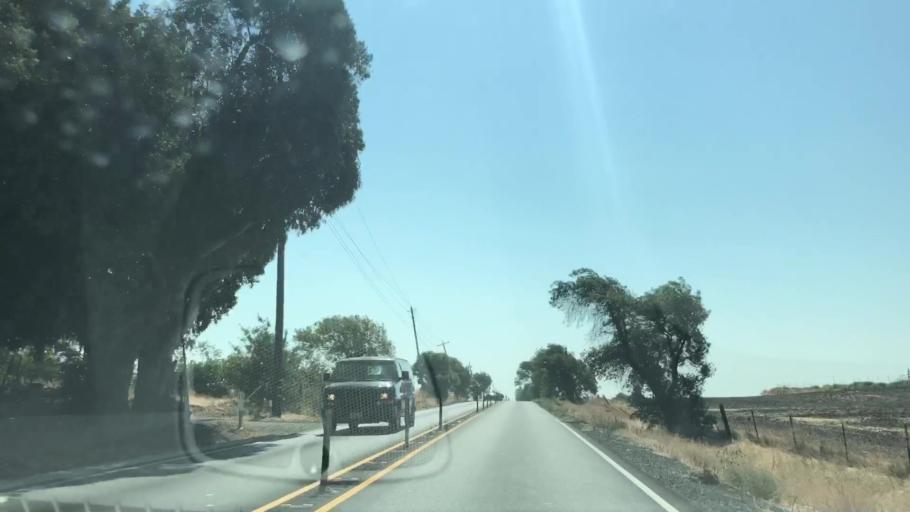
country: US
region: California
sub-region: Solano County
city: Rio Vista
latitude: 38.1735
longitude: -121.7131
